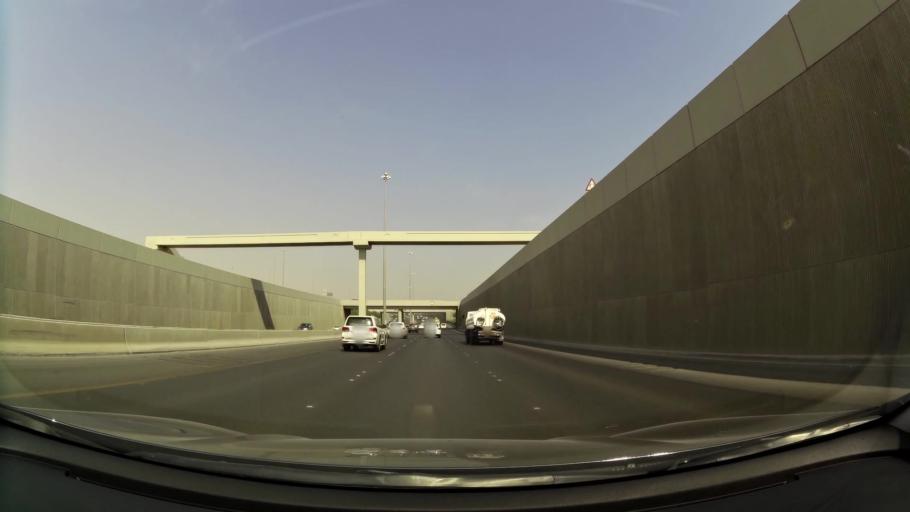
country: KW
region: Al Ahmadi
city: Al Manqaf
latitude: 29.1048
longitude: 48.1180
